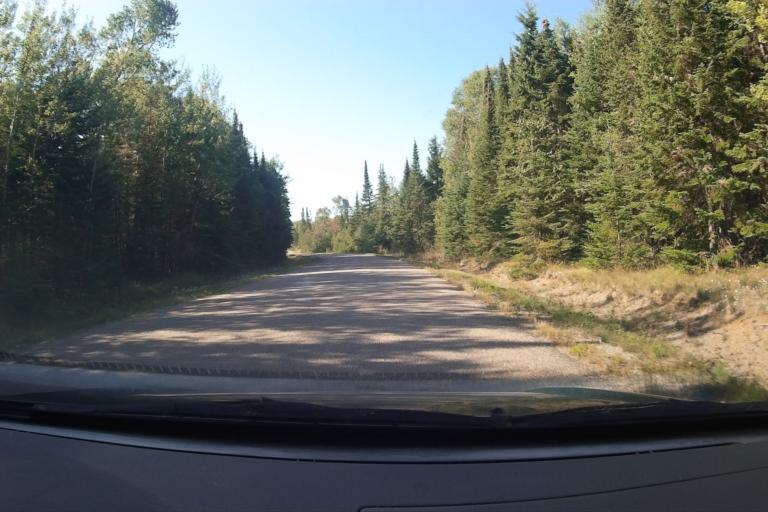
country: CA
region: Ontario
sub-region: Thunder Bay District
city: Thunder Bay
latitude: 48.3552
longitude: -88.8029
